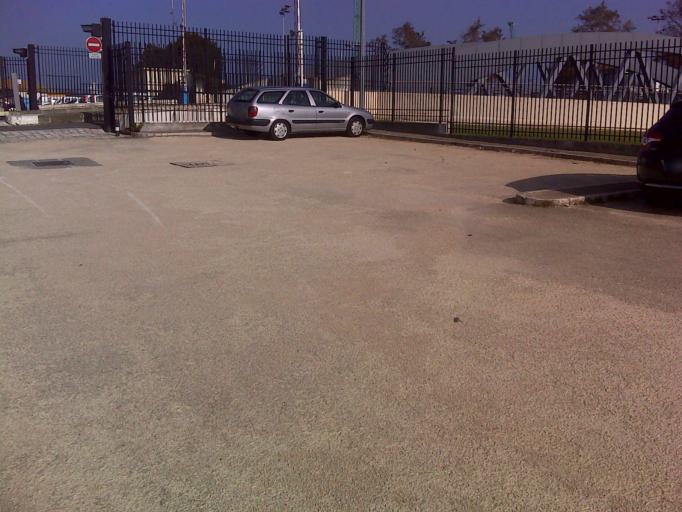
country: FR
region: Poitou-Charentes
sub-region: Departement de la Charente-Maritime
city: Rochefort
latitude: 45.9462
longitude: -0.9541
